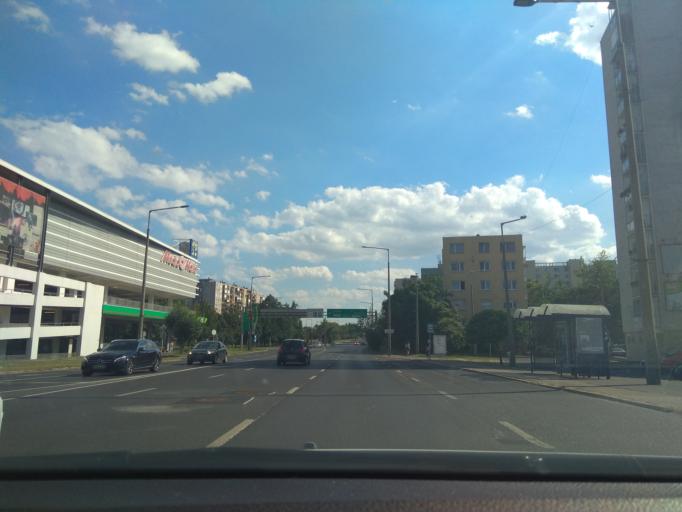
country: HU
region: Borsod-Abauj-Zemplen
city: Miskolc
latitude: 48.1019
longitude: 20.7918
